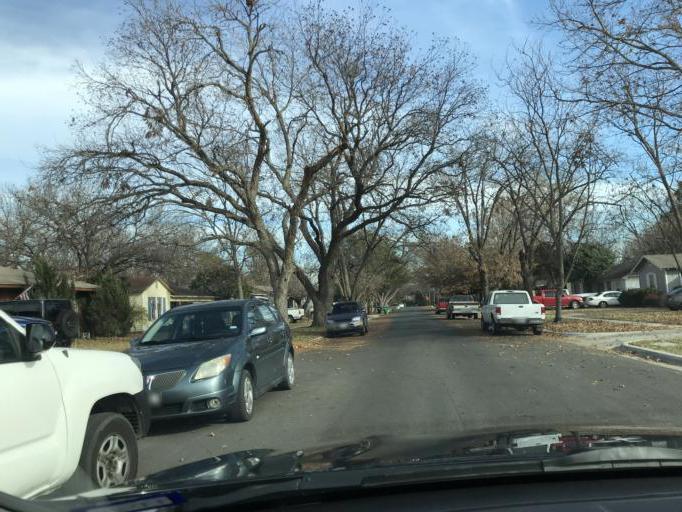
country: US
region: Texas
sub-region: Denton County
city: Denton
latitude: 33.2276
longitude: -97.1400
